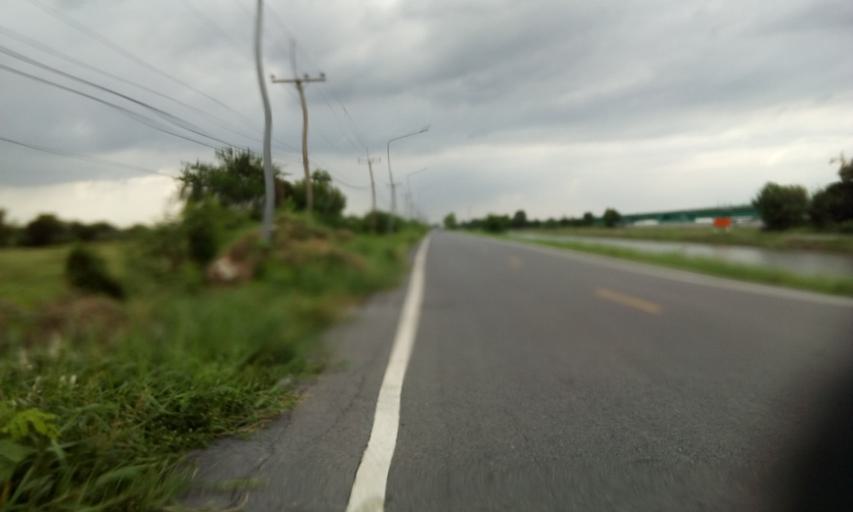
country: TH
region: Pathum Thani
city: Nong Suea
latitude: 14.0652
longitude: 100.8464
